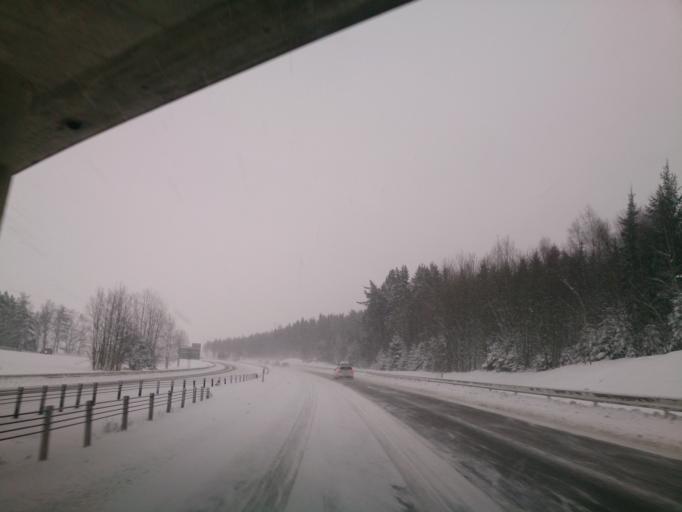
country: SE
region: Soedermanland
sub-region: Nykopings Kommun
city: Svalsta
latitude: 58.7460
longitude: 16.9319
